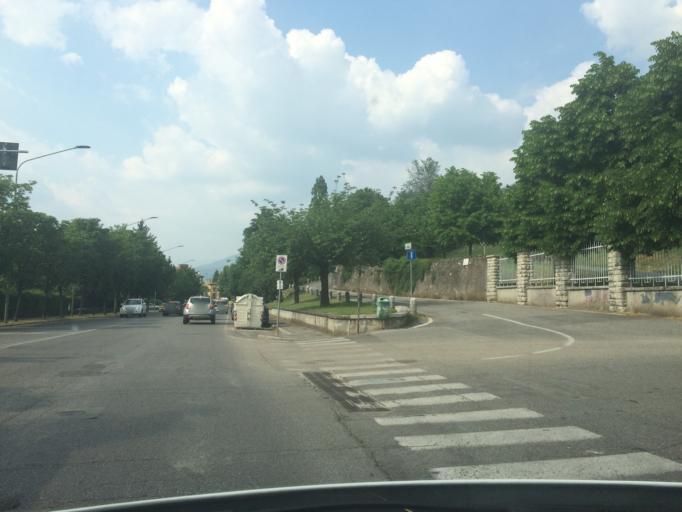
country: IT
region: Lombardy
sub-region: Provincia di Brescia
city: Brescia
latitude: 45.5469
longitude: 10.2292
